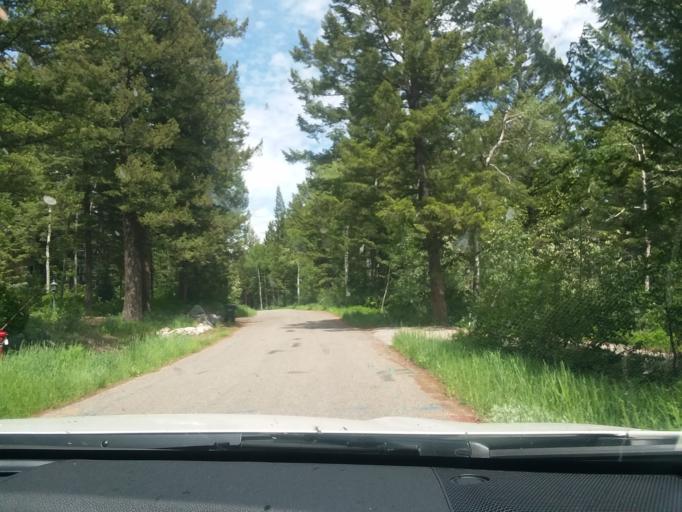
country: US
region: Wyoming
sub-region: Teton County
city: Moose Wilson Road
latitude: 43.5872
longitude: -110.8365
